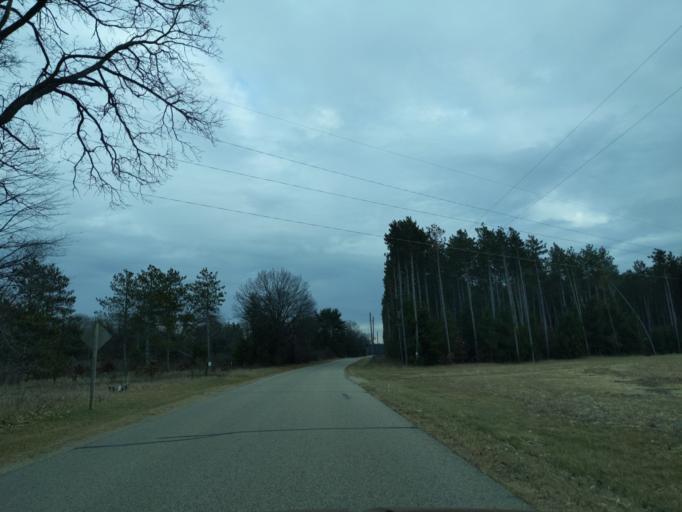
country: US
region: Wisconsin
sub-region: Waushara County
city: Wautoma
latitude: 44.0471
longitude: -89.2929
